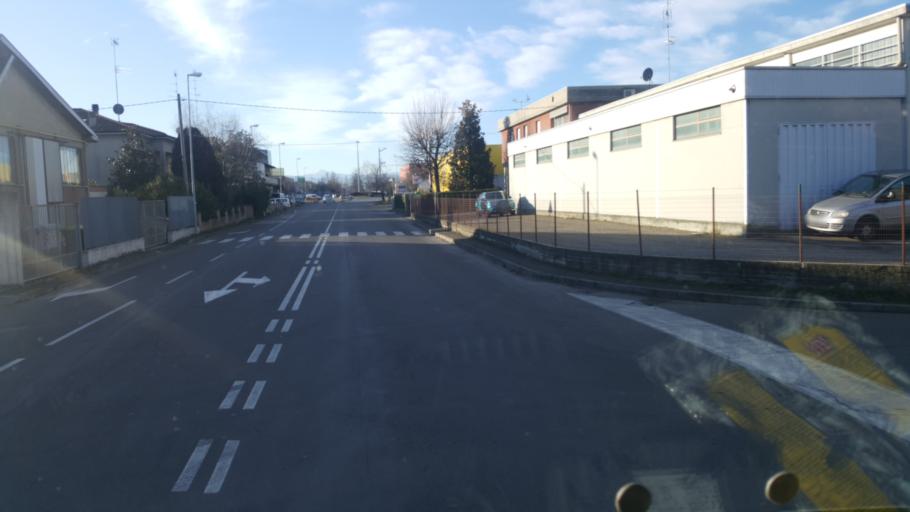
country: IT
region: Emilia-Romagna
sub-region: Provincia di Reggio Emilia
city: Rubiera
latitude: 44.6564
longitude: 10.7740
